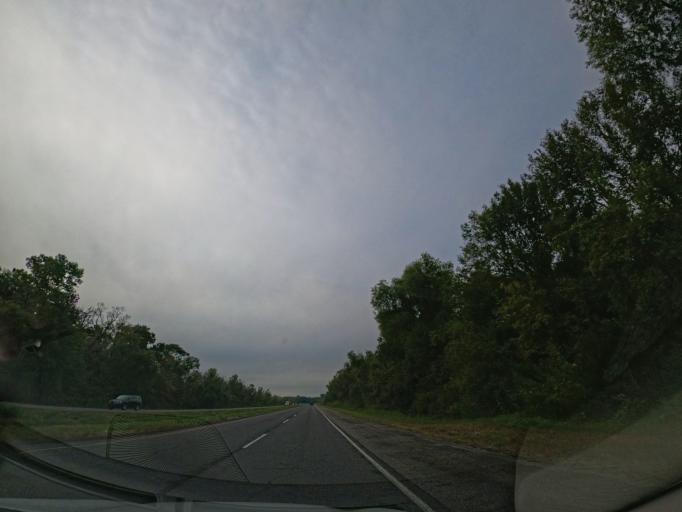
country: US
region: Louisiana
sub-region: Terrebonne Parish
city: Houma
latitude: 29.6310
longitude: -90.6621
